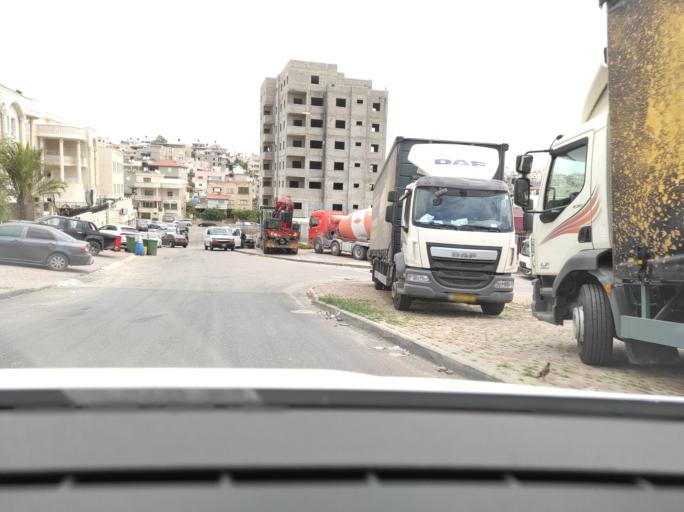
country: IL
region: Central District
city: Kafr Qasim
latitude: 32.1140
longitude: 34.9670
